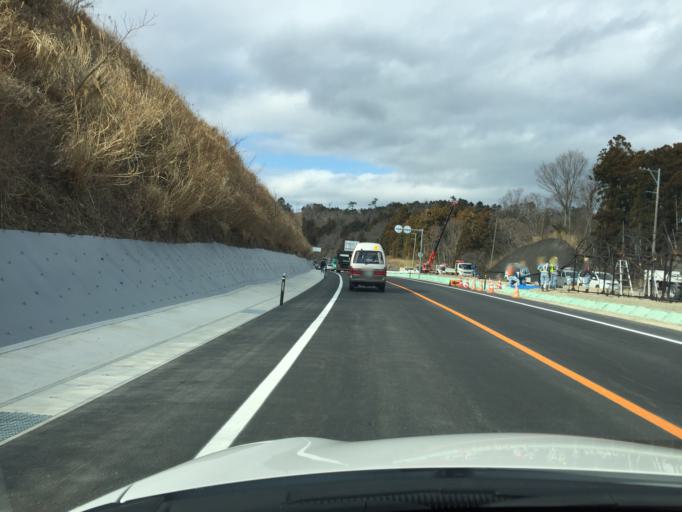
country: JP
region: Fukushima
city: Iwaki
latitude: 37.1574
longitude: 140.9954
